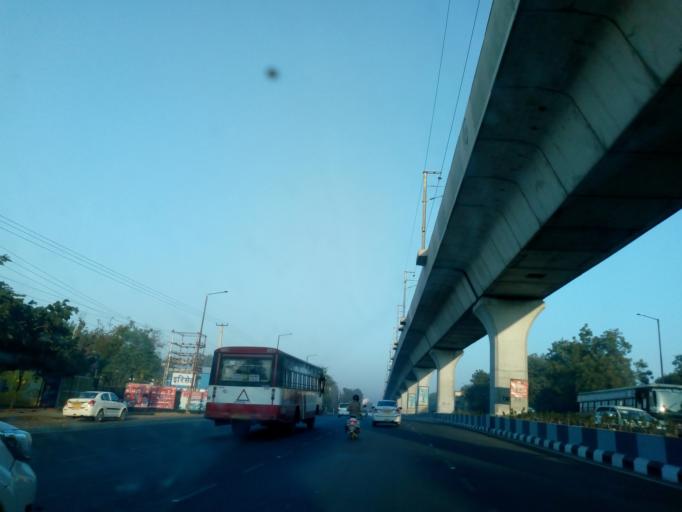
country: IN
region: Telangana
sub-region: Hyderabad
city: Malkajgiri
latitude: 17.4311
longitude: 78.5245
